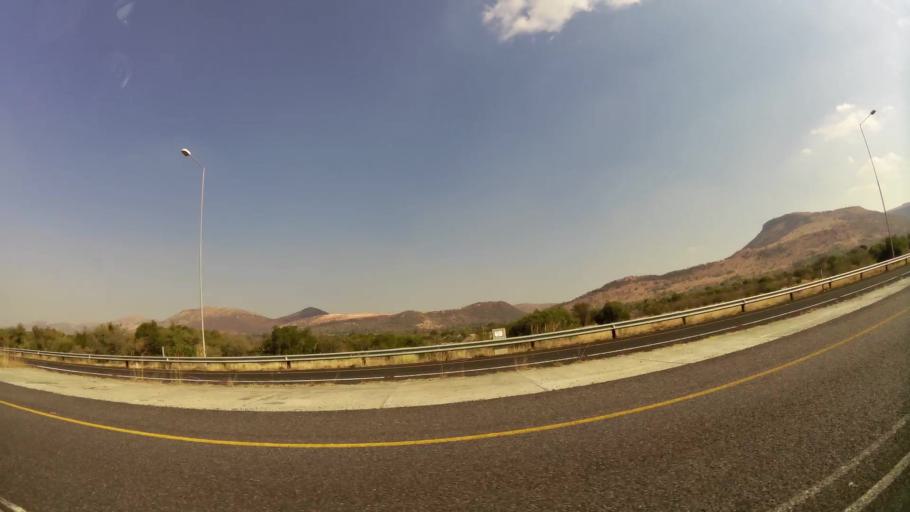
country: ZA
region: North-West
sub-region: Bojanala Platinum District Municipality
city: Rustenburg
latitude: -25.6098
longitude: 27.1480
